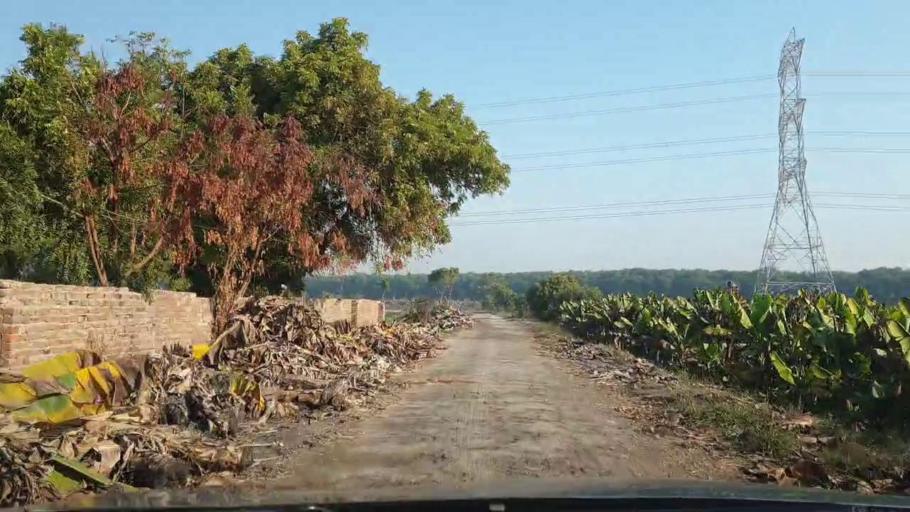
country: PK
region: Sindh
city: Tando Allahyar
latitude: 25.4921
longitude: 68.7111
